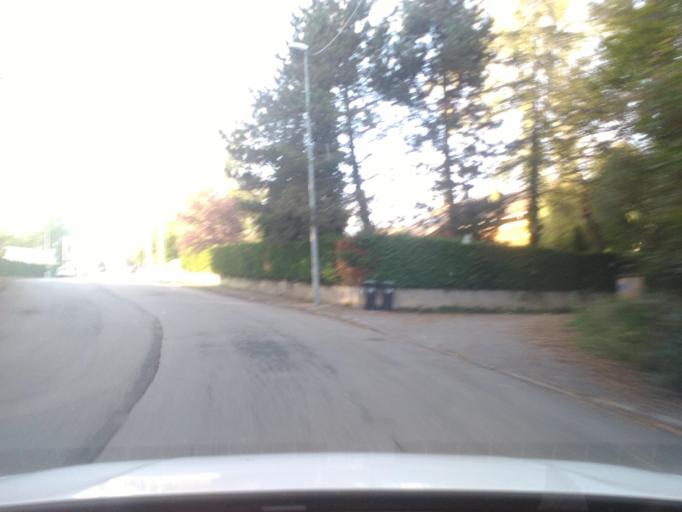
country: FR
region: Lorraine
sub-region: Departement des Vosges
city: Saint-Die-des-Vosges
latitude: 48.2961
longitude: 6.9501
